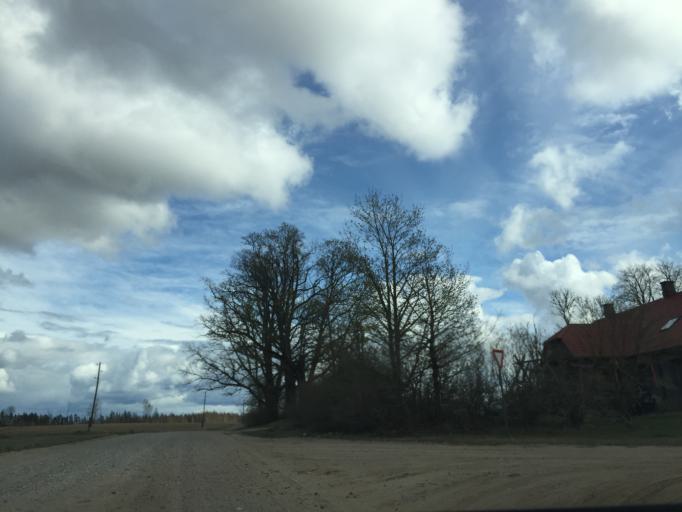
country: LV
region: Limbazu Rajons
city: Limbazi
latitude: 57.6075
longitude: 24.7935
